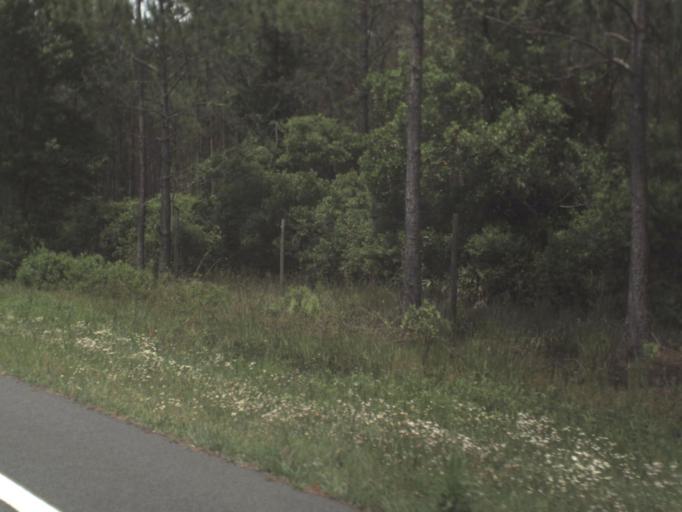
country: US
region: Florida
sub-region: Hamilton County
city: Jasper
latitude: 30.5115
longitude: -82.6692
